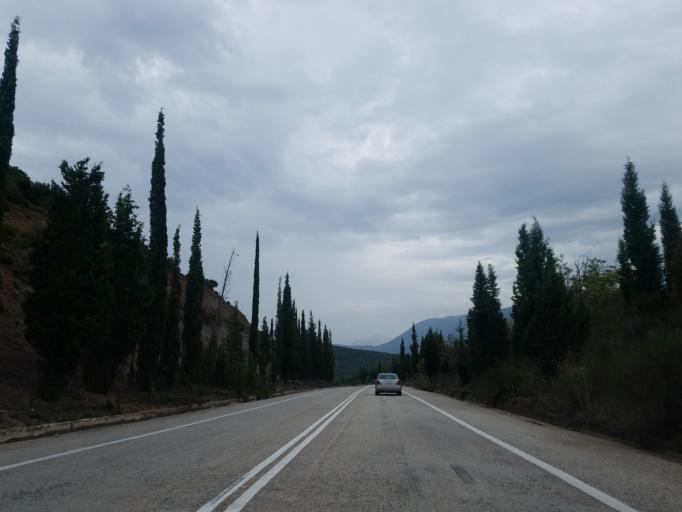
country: GR
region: Central Greece
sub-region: Nomos Voiotias
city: Livadeia
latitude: 38.4427
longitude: 22.8071
